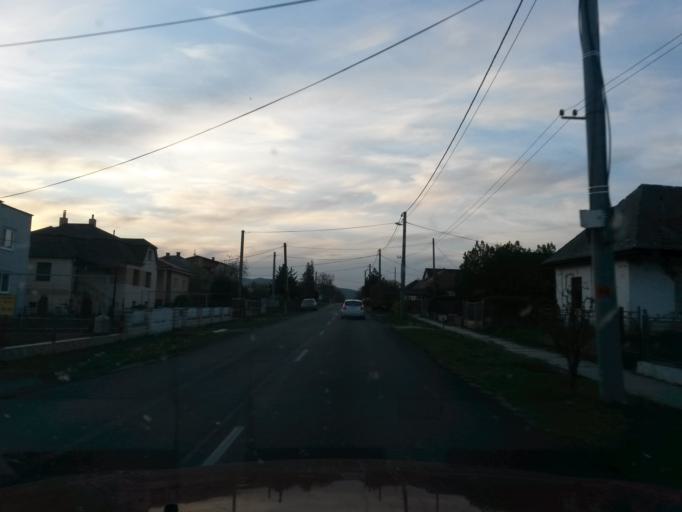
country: HU
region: Borsod-Abauj-Zemplen
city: Satoraljaujhely
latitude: 48.5312
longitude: 21.5796
